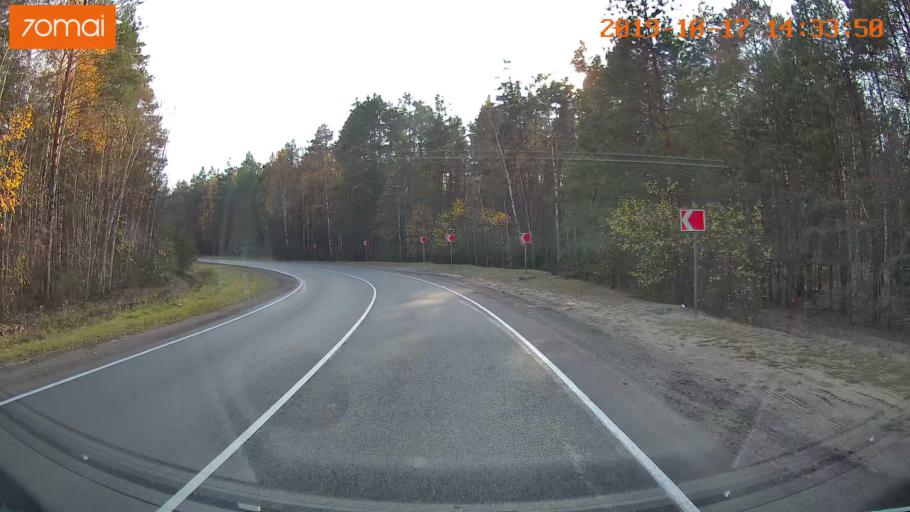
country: RU
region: Rjazan
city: Solotcha
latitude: 54.9192
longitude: 39.9966
